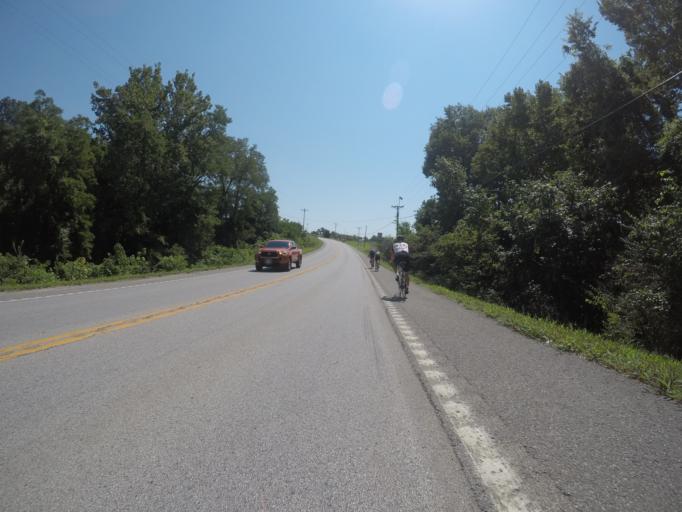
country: US
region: Missouri
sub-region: Platte County
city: Weston
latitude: 39.4250
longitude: -94.9052
